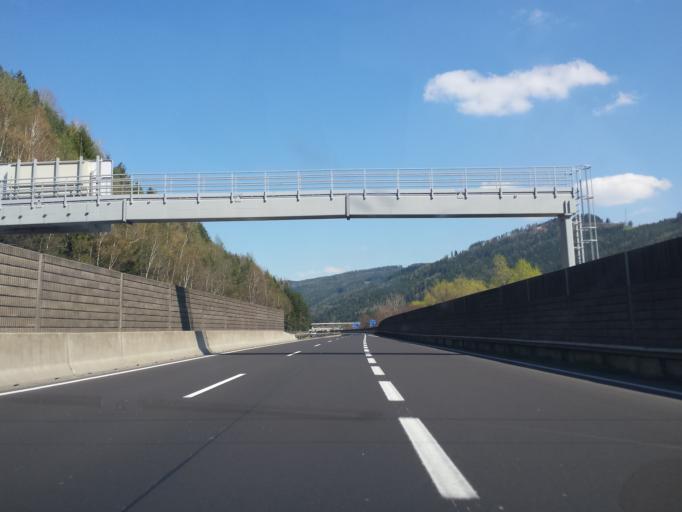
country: AT
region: Styria
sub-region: Politischer Bezirk Leoben
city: Sankt Michael in Obersteiermark
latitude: 47.3423
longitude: 15.0071
